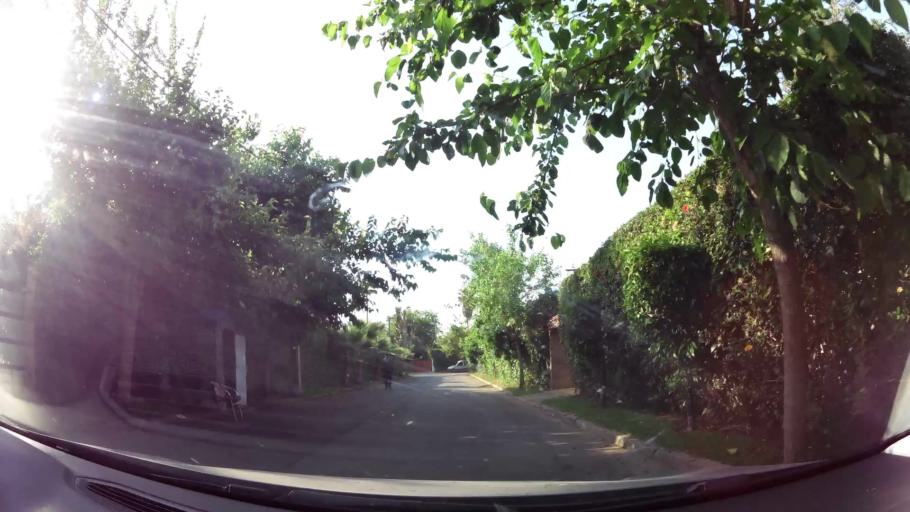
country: MA
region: Rabat-Sale-Zemmour-Zaer
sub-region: Rabat
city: Rabat
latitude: 33.9380
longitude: -6.8100
